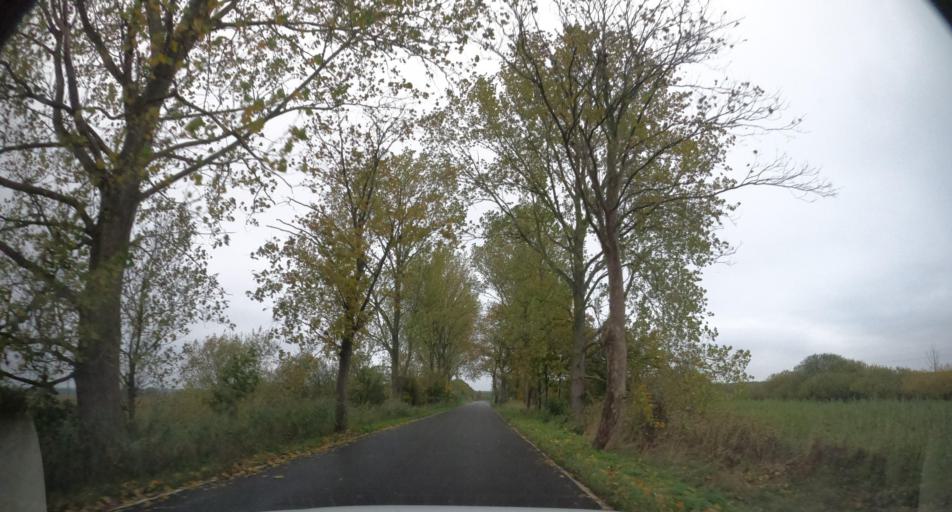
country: PL
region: West Pomeranian Voivodeship
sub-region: Powiat kamienski
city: Wolin
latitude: 53.9248
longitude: 14.6090
